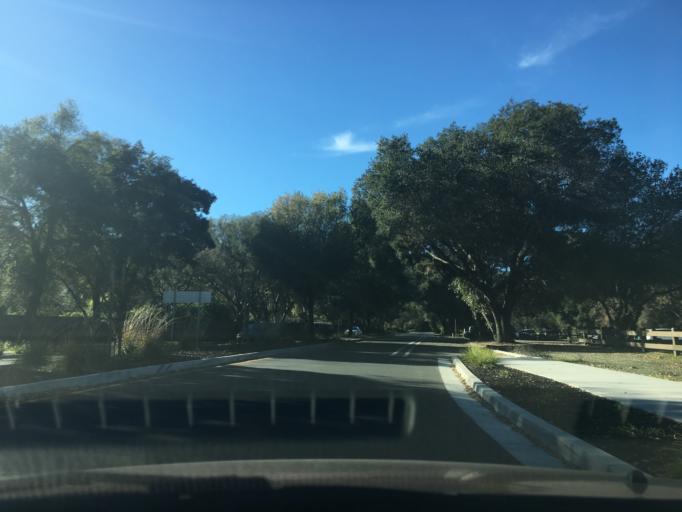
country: US
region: California
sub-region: Contra Costa County
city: Saranap
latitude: 37.8861
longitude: -122.0933
